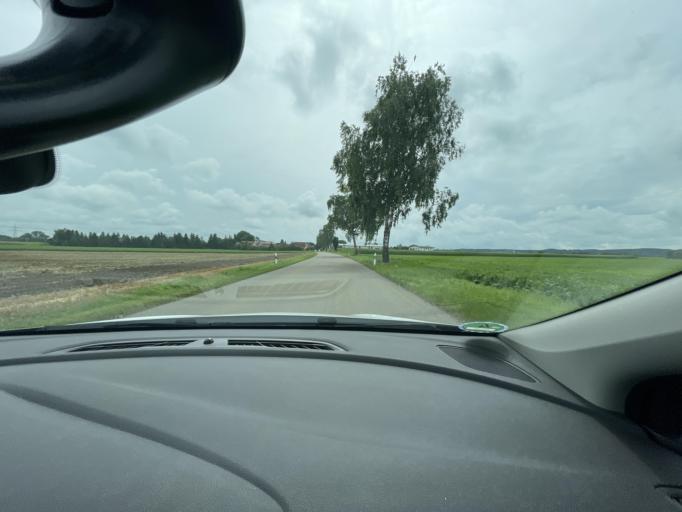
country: DE
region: Bavaria
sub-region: Swabia
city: Ellgau
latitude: 48.5833
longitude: 10.8585
